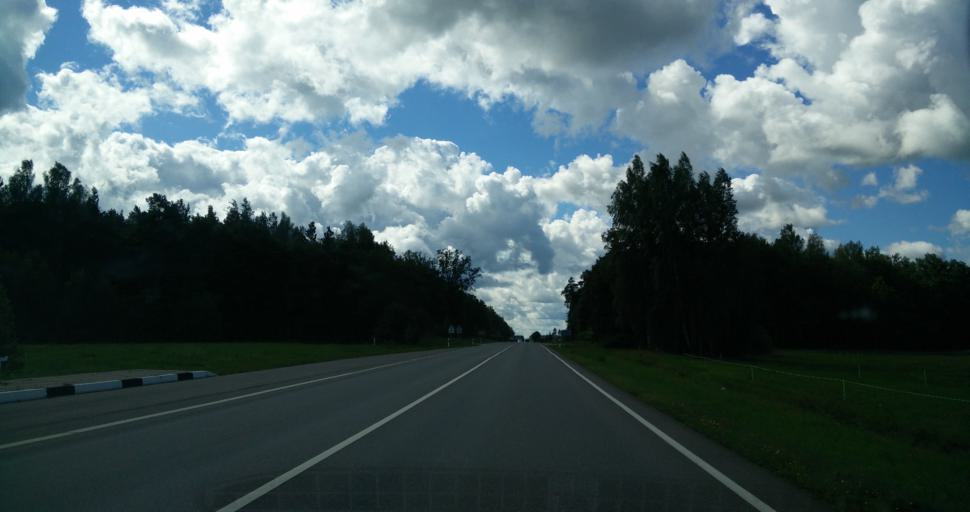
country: LT
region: Klaipedos apskritis
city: Silute
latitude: 55.4165
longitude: 21.4813
